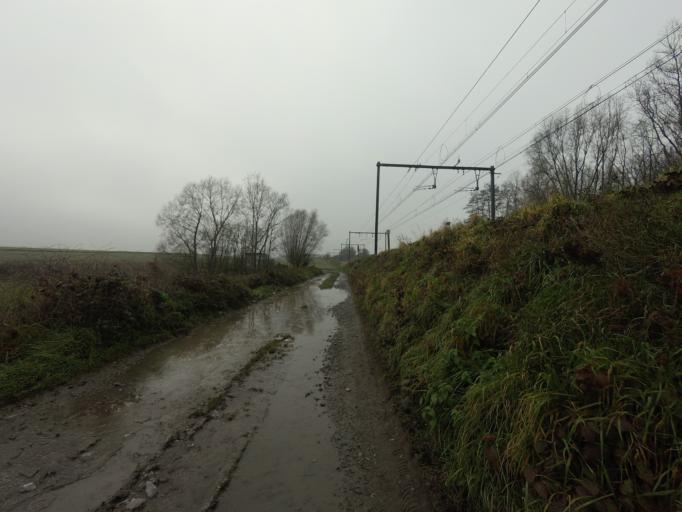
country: BE
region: Flanders
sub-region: Provincie Oost-Vlaanderen
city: Geraardsbergen
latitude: 50.7900
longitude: 3.8821
